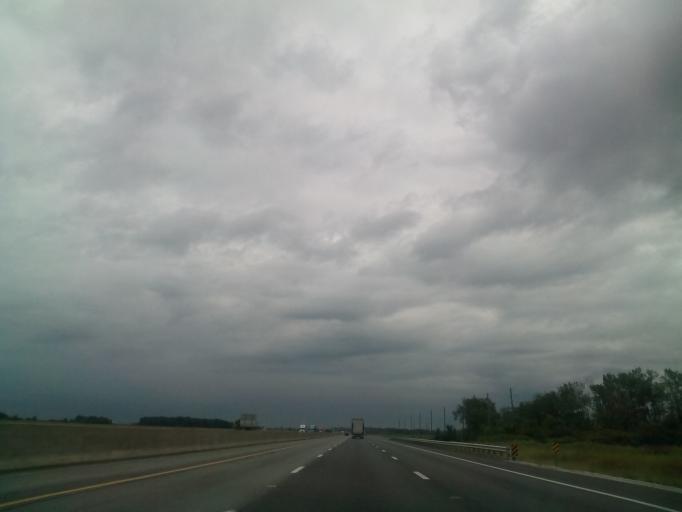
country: US
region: Ohio
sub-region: Sandusky County
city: Woodville
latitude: 41.4813
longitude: -83.3490
